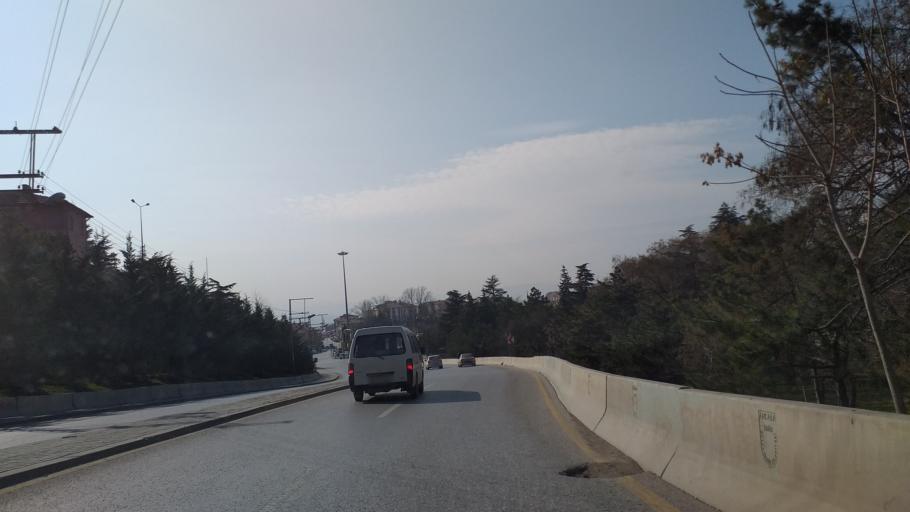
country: TR
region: Ankara
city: Mamak
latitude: 40.0016
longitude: 32.8561
